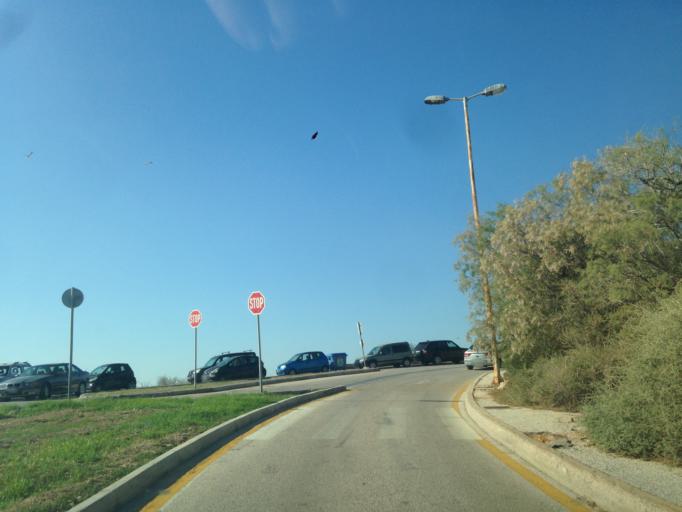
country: GR
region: Attica
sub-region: Nomarchia Anatolikis Attikis
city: Vouliagmeni
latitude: 37.7992
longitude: 23.7724
